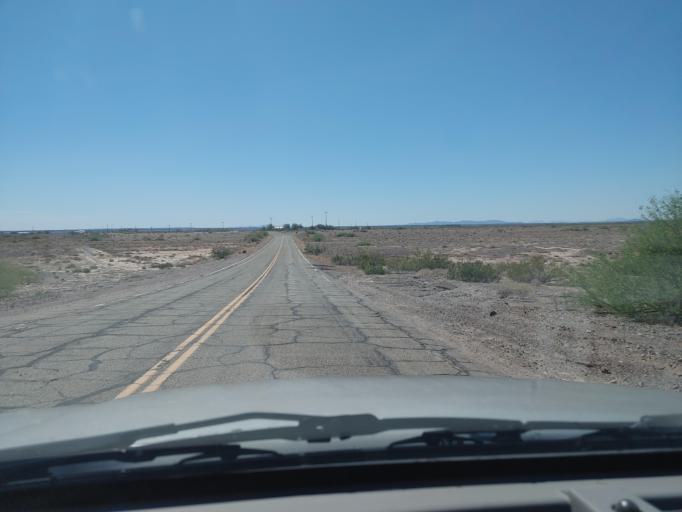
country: US
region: Arizona
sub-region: Maricopa County
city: Gila Bend
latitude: 32.9972
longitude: -113.3412
